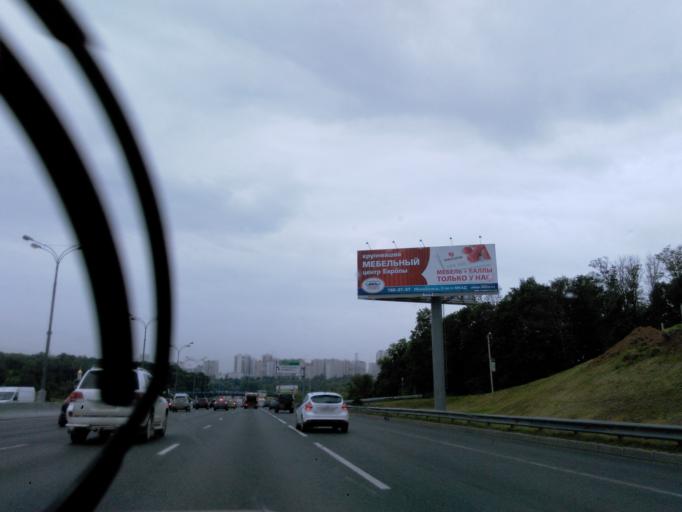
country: RU
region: Moscow
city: Strogino
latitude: 55.8562
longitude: 37.3959
